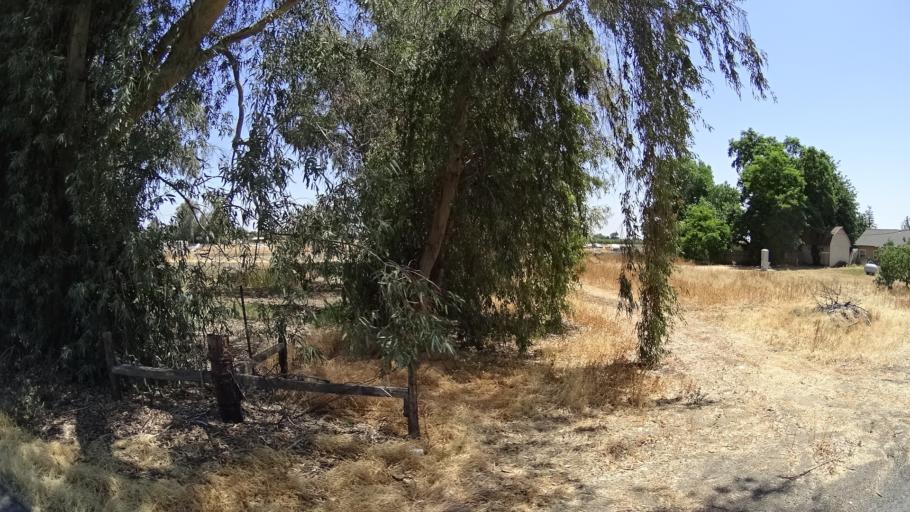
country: US
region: California
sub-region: Kings County
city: Lemoore
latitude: 36.2727
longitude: -119.7629
